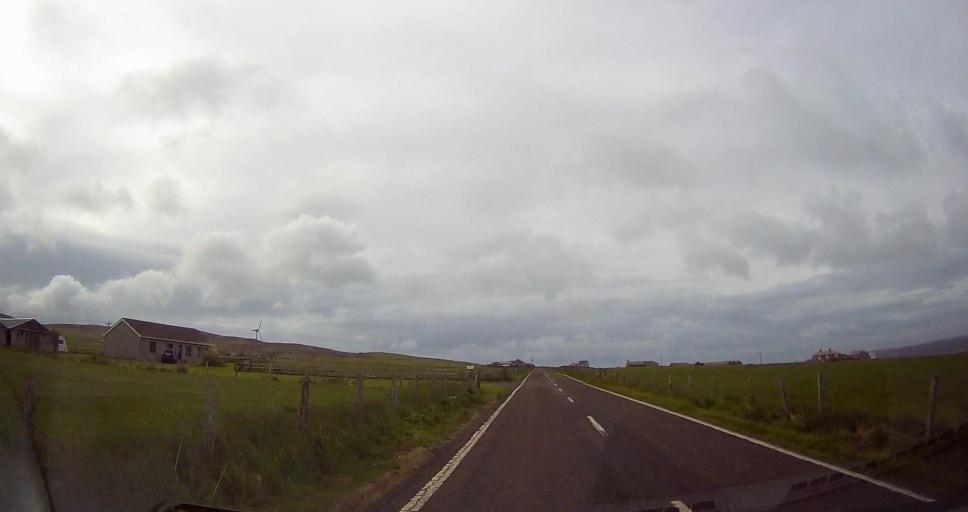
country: GB
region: Scotland
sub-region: Orkney Islands
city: Stromness
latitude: 58.9360
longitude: -3.2103
